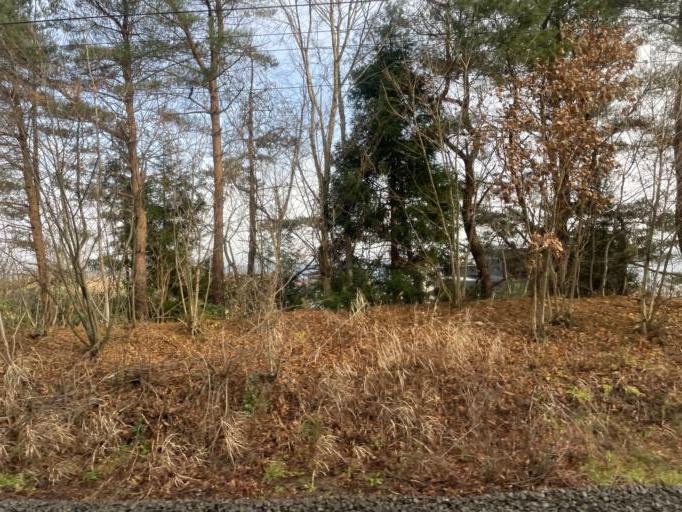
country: JP
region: Aomori
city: Aomori Shi
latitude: 40.9183
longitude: 141.0310
